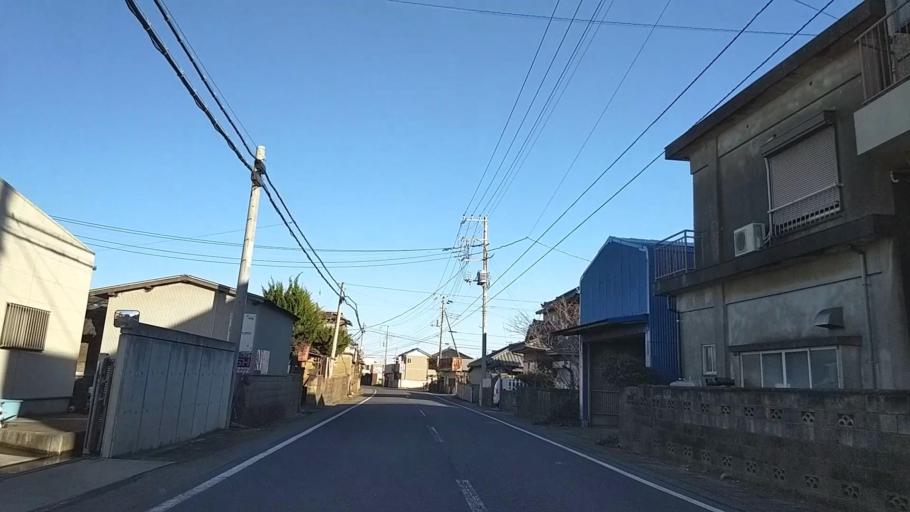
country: JP
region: Chiba
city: Asahi
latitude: 35.6891
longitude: 140.6501
